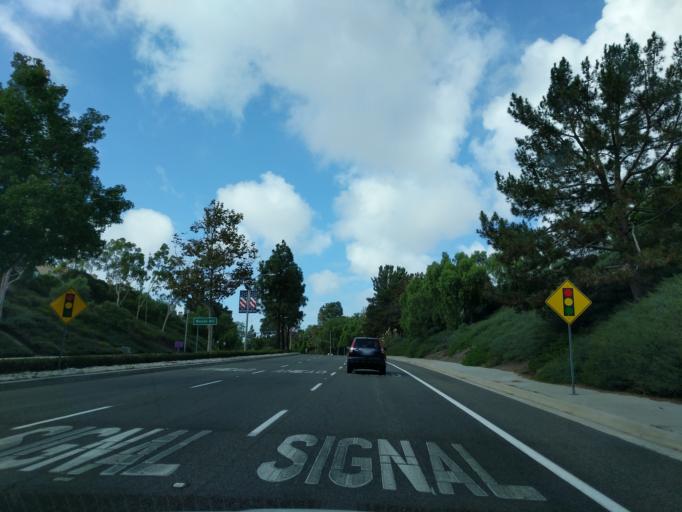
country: US
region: California
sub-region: Orange County
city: Laguna Niguel
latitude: 33.5050
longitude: -117.6892
